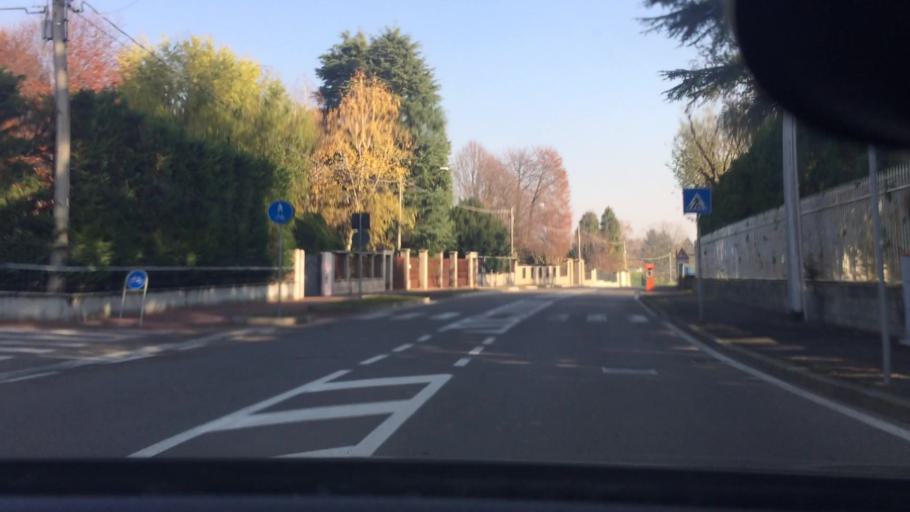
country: IT
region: Lombardy
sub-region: Provincia di Como
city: Manera
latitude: 45.6661
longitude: 9.0411
